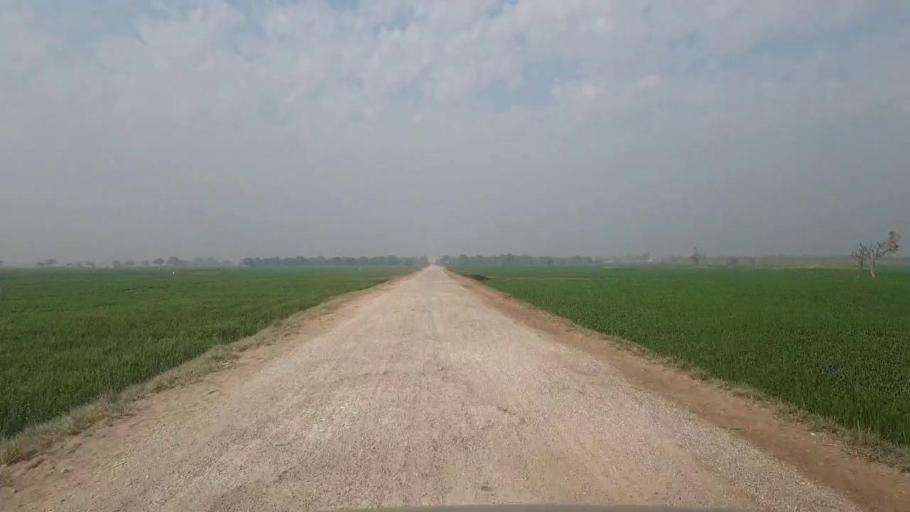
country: PK
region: Sindh
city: Hala
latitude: 25.9074
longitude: 68.4409
